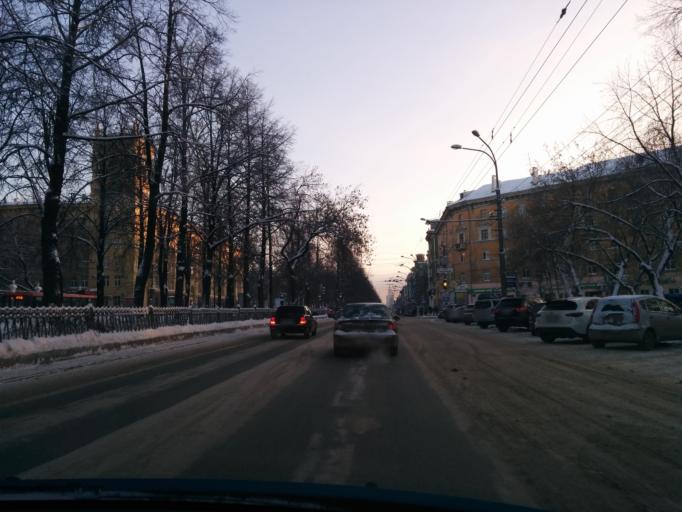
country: RU
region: Perm
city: Perm
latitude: 58.0032
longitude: 56.2464
